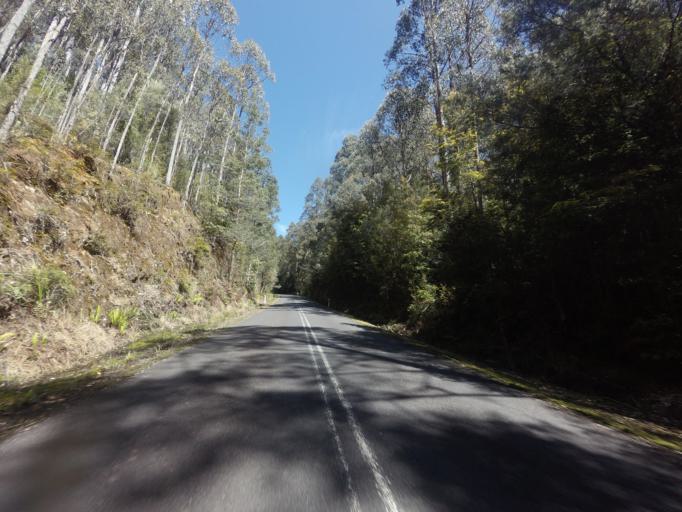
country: AU
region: Tasmania
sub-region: Huon Valley
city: Geeveston
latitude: -42.8241
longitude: 146.3314
